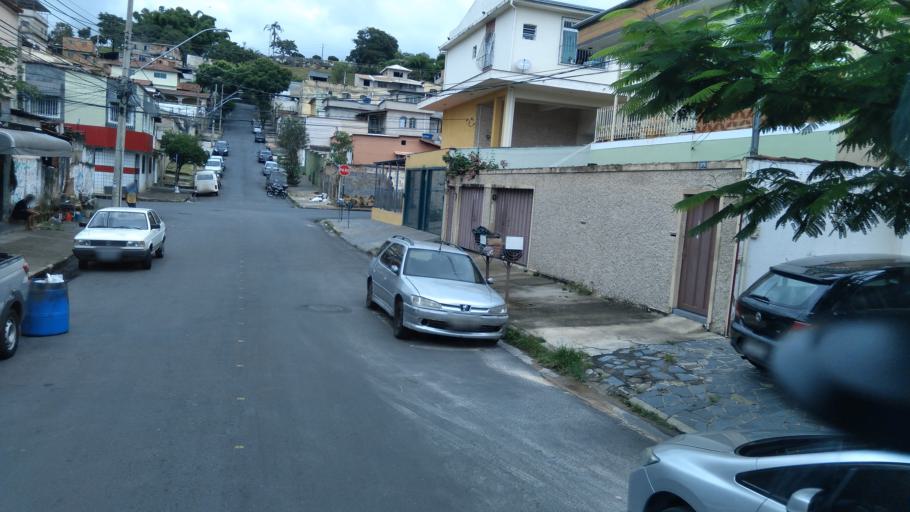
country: BR
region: Minas Gerais
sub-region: Belo Horizonte
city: Belo Horizonte
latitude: -19.9144
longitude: -43.8961
